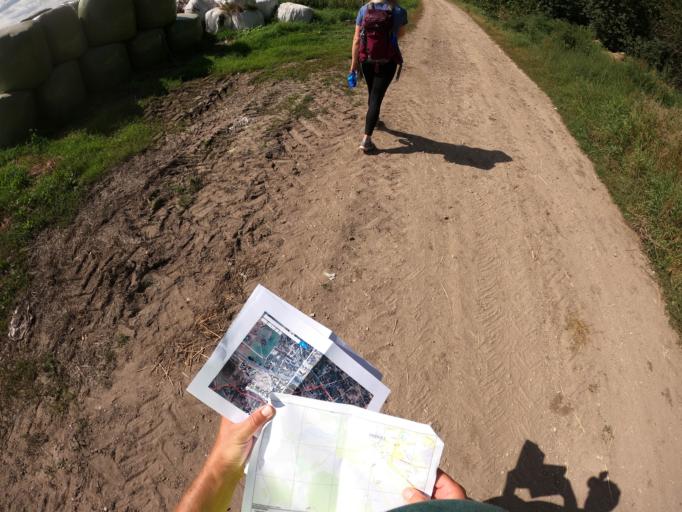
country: LV
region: Priekule
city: Priekule
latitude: 56.4346
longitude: 21.5674
